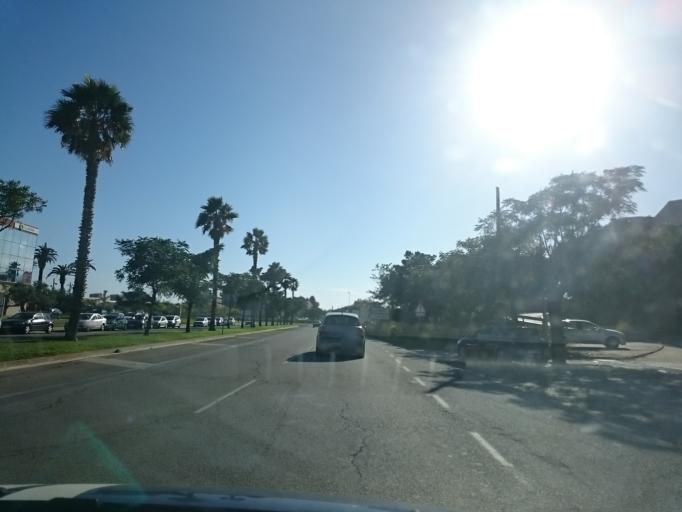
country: ES
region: Catalonia
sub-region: Provincia de Barcelona
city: Viladecans
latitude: 41.3241
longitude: 2.0312
